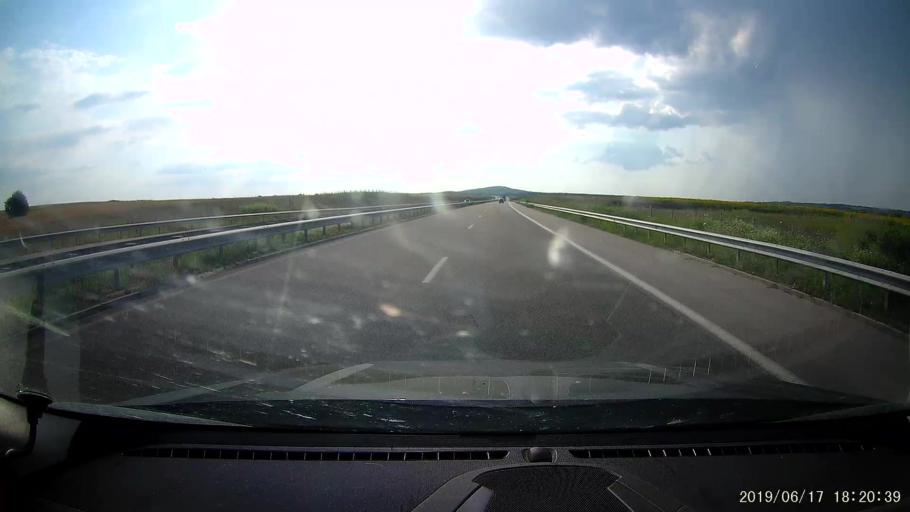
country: BG
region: Khaskovo
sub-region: Obshtina Simeonovgrad
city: Simeonovgrad
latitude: 41.9630
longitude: 25.8067
